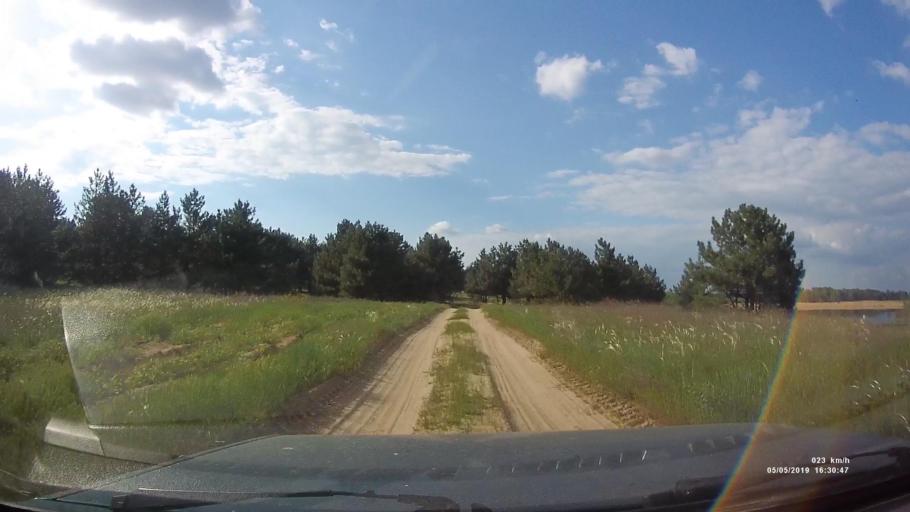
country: RU
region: Rostov
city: Ust'-Donetskiy
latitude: 47.7747
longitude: 41.0157
